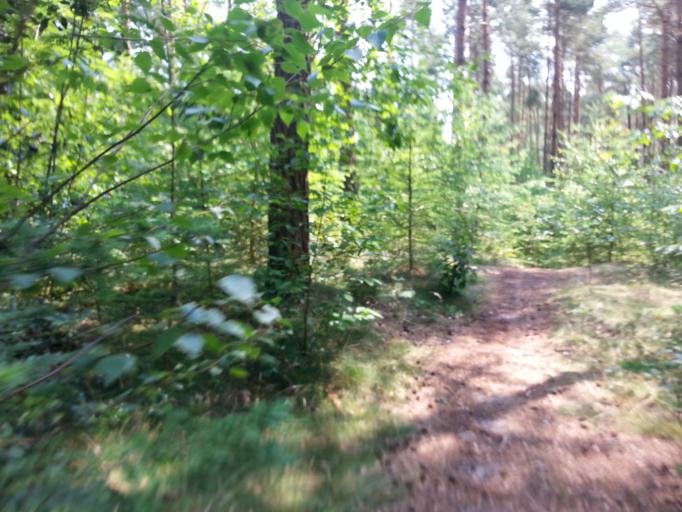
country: NL
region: Utrecht
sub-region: Gemeente Amersfoort
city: Randenbroek
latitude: 52.1270
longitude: 5.3888
